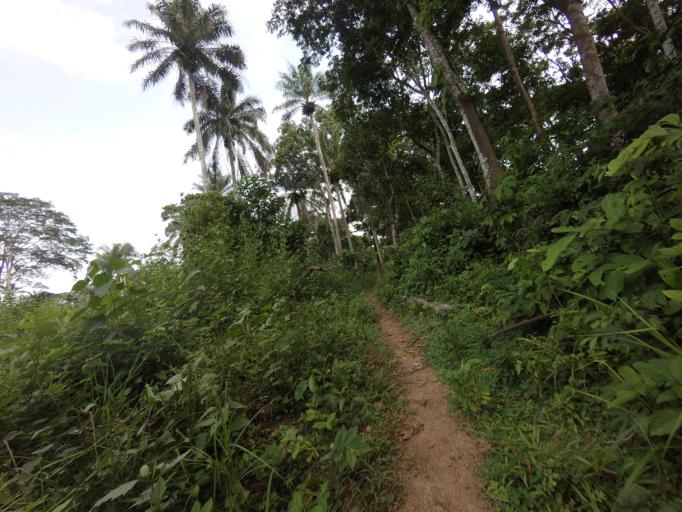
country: SL
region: Eastern Province
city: Tombodu
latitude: 8.1592
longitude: -10.6289
